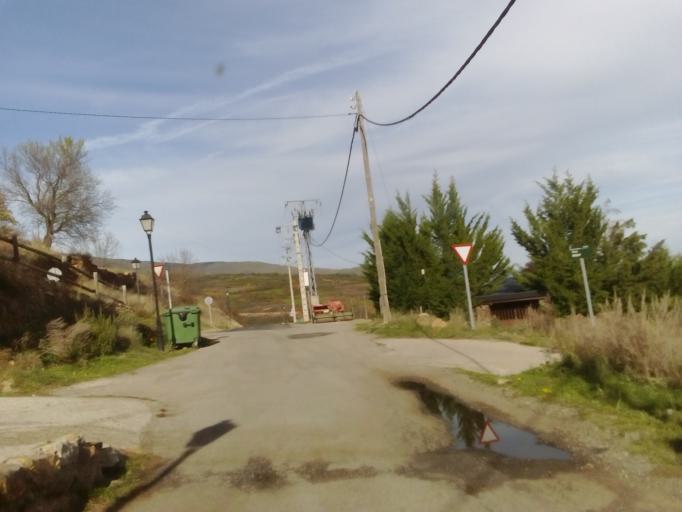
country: ES
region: Catalonia
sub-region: Provincia de Lleida
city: Eller
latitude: 42.3983
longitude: 1.8017
